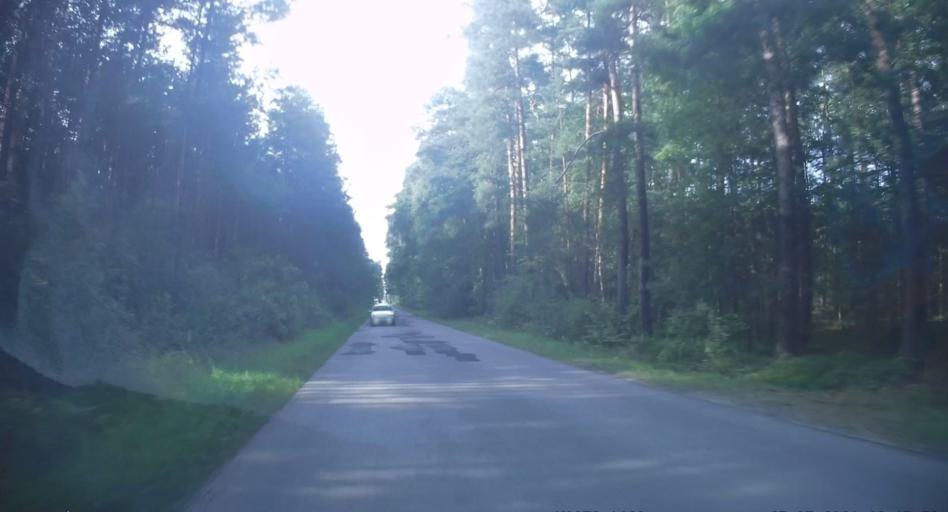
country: PL
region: Swietokrzyskie
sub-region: Powiat konecki
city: Konskie
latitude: 51.2303
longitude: 20.3830
